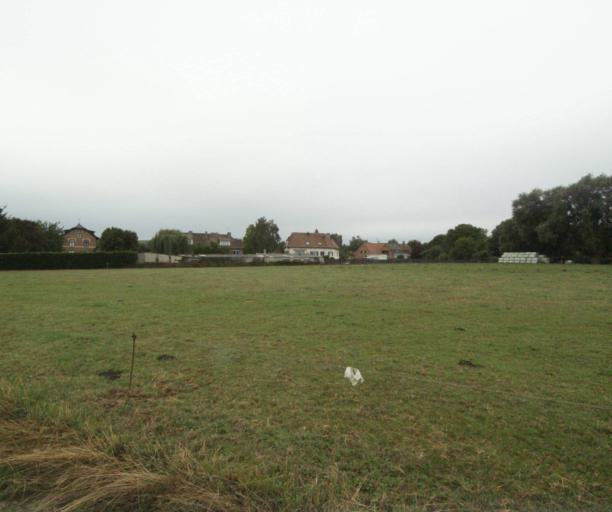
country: FR
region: Nord-Pas-de-Calais
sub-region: Departement du Nord
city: Willems
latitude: 50.6241
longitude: 3.2348
